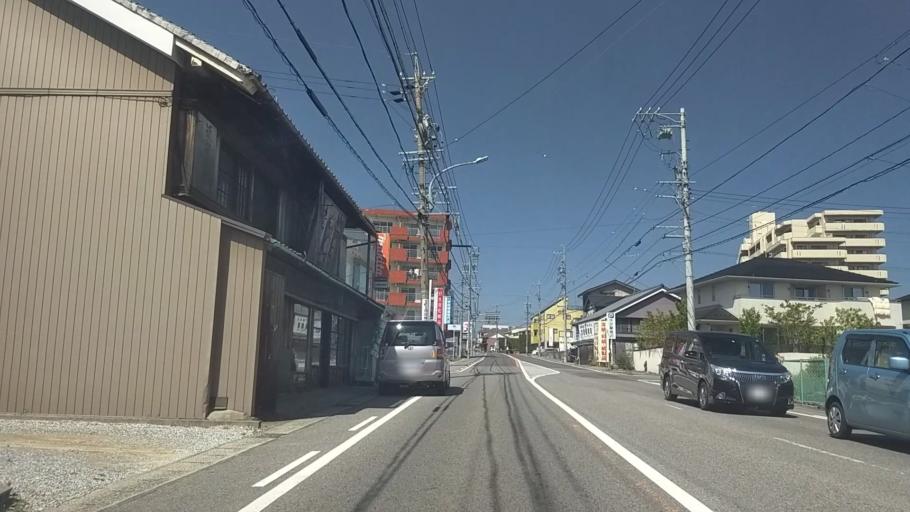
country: JP
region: Aichi
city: Okazaki
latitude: 34.9722
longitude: 137.1670
